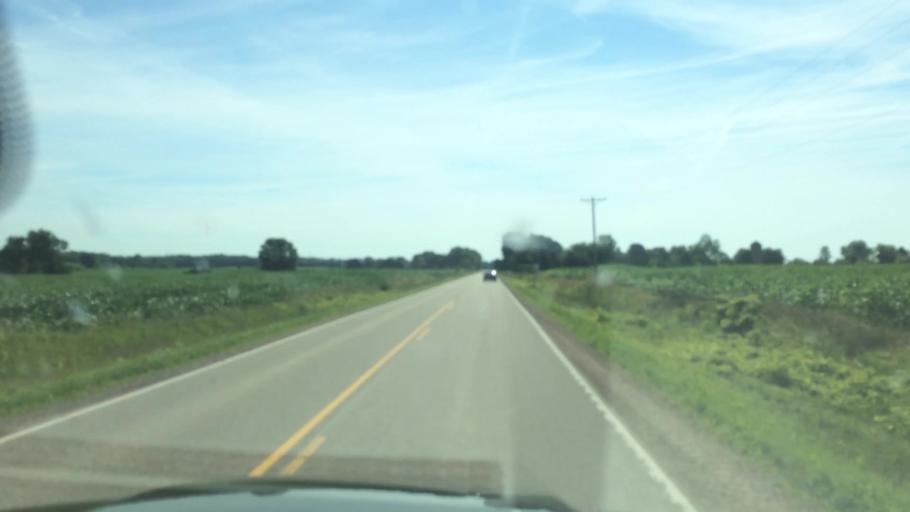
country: US
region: Wisconsin
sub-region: Oconto County
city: Gillett
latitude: 44.7875
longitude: -88.3301
